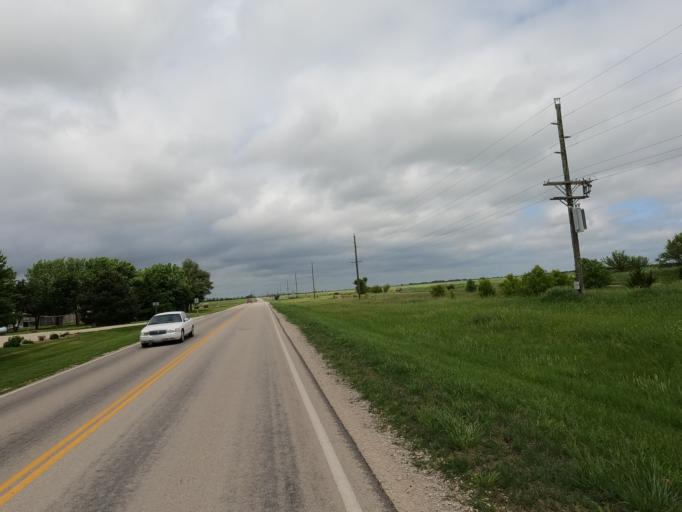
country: US
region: Kansas
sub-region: McPherson County
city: McPherson
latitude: 38.2926
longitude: -97.6290
